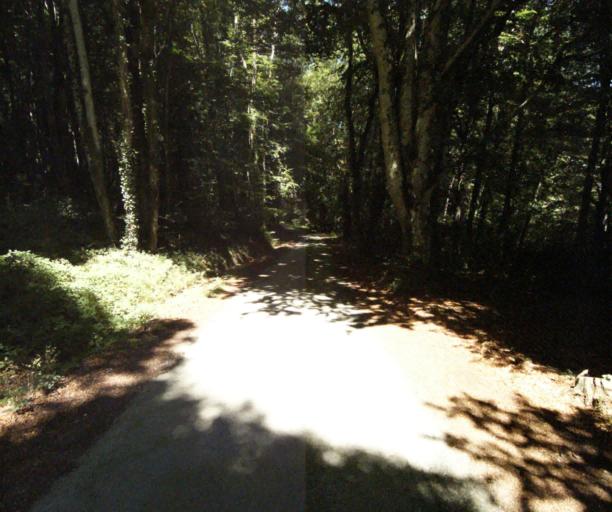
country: FR
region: Midi-Pyrenees
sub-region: Departement du Tarn
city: Dourgne
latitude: 43.4314
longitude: 2.1584
